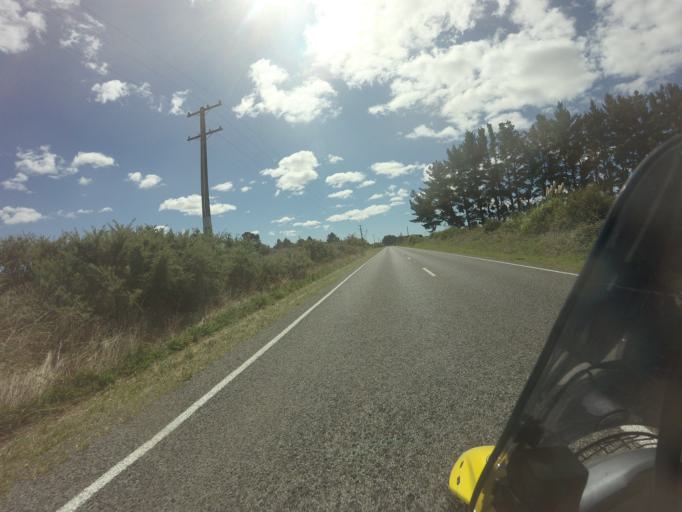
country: NZ
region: Bay of Plenty
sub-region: Whakatane District
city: Edgecumbe
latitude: -38.0759
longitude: 176.8179
